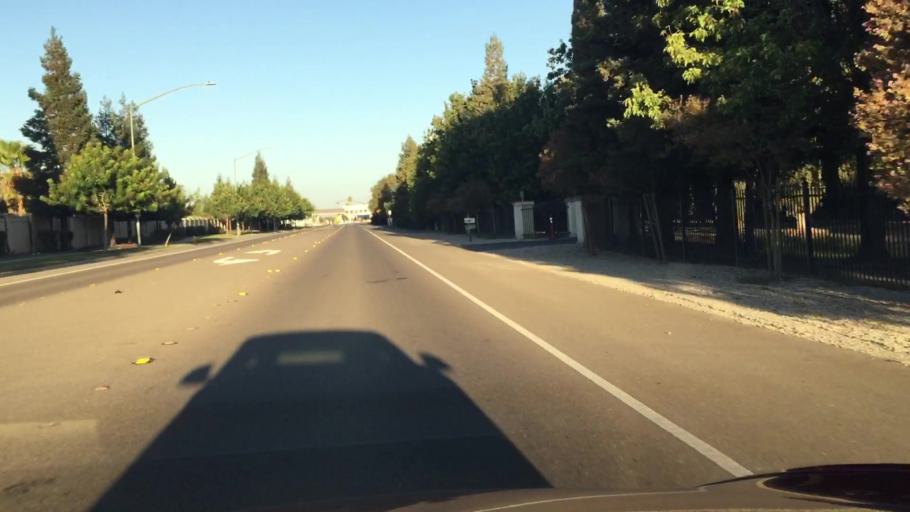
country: US
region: California
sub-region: San Joaquin County
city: Tracy
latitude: 37.7107
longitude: -121.4014
